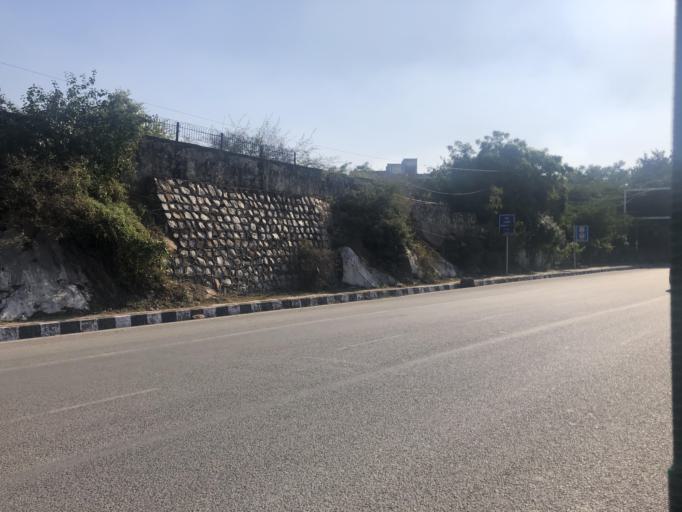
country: IN
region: NCT
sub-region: Central Delhi
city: Karol Bagh
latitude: 28.5433
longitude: 77.1589
